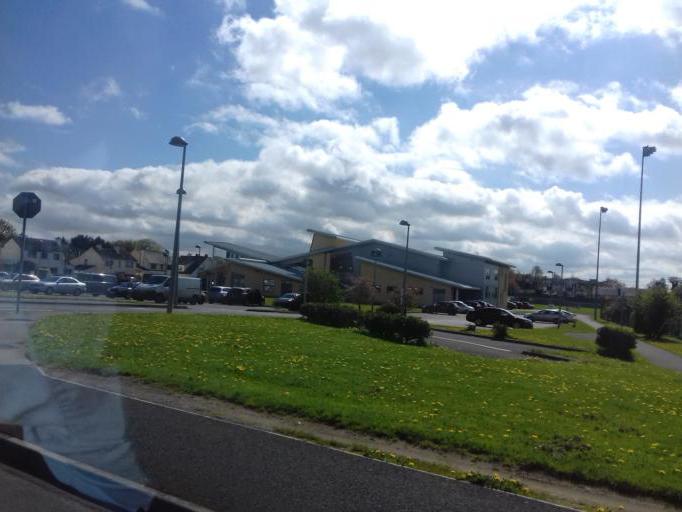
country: IE
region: Leinster
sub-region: Laois
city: Portlaoise
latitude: 53.0390
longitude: -7.2951
